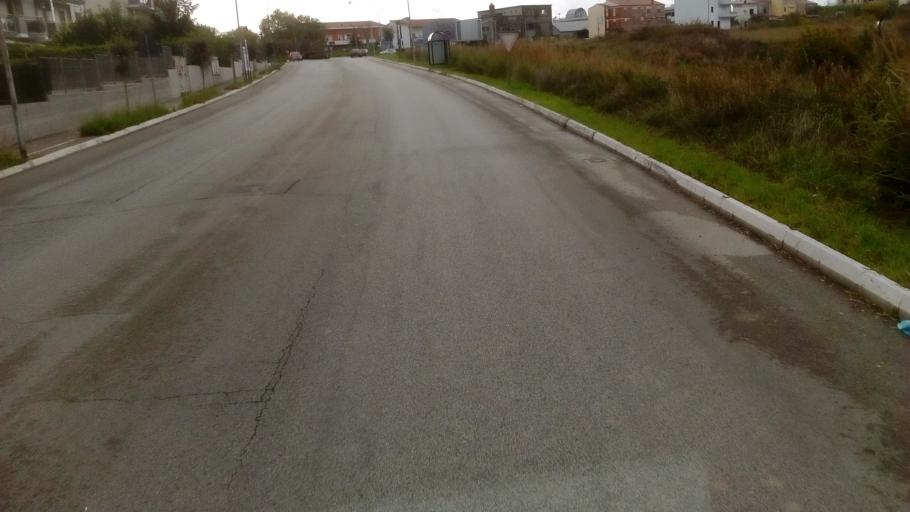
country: IT
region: Abruzzo
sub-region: Provincia di Chieti
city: Vasto
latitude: 42.1025
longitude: 14.7021
